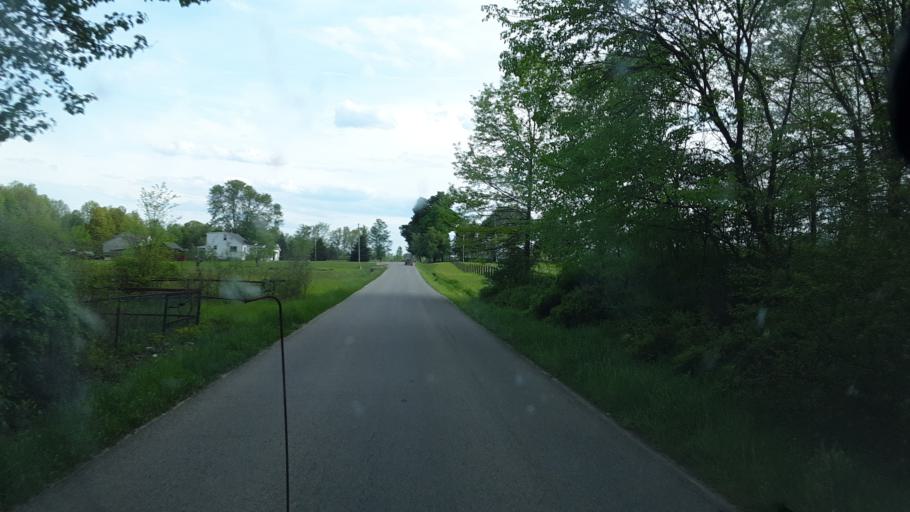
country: US
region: Ohio
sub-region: Portage County
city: Windham
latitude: 41.2509
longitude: -81.0667
